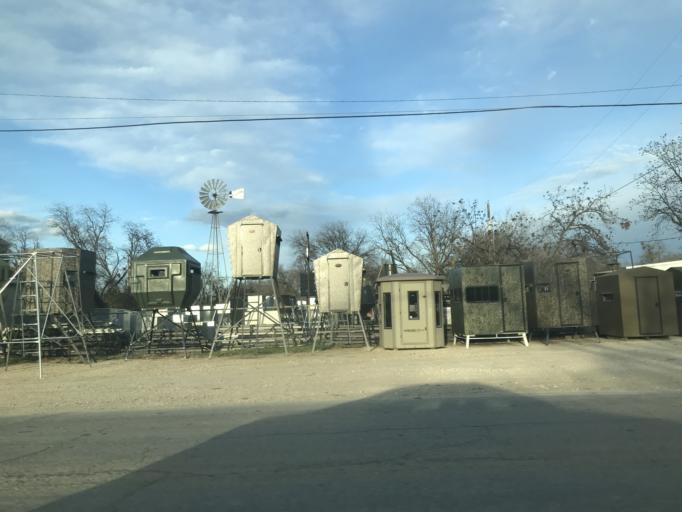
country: US
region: Texas
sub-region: Tom Green County
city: San Angelo
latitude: 31.4956
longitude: -100.4582
